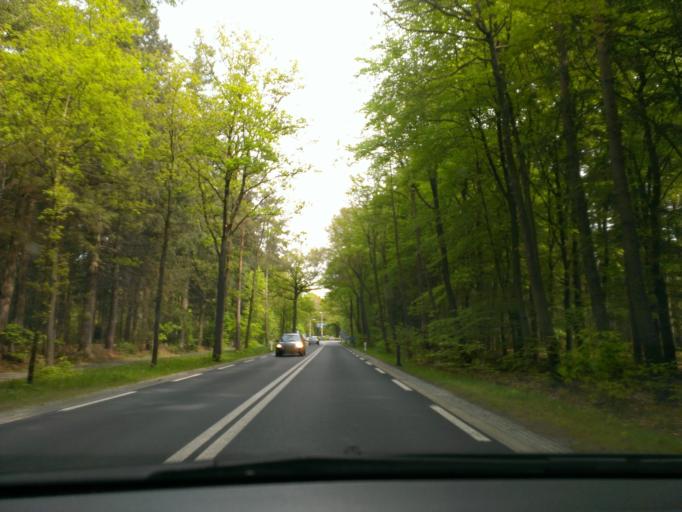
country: NL
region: Gelderland
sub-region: Gemeente Epe
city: Epe
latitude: 52.3601
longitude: 5.9230
